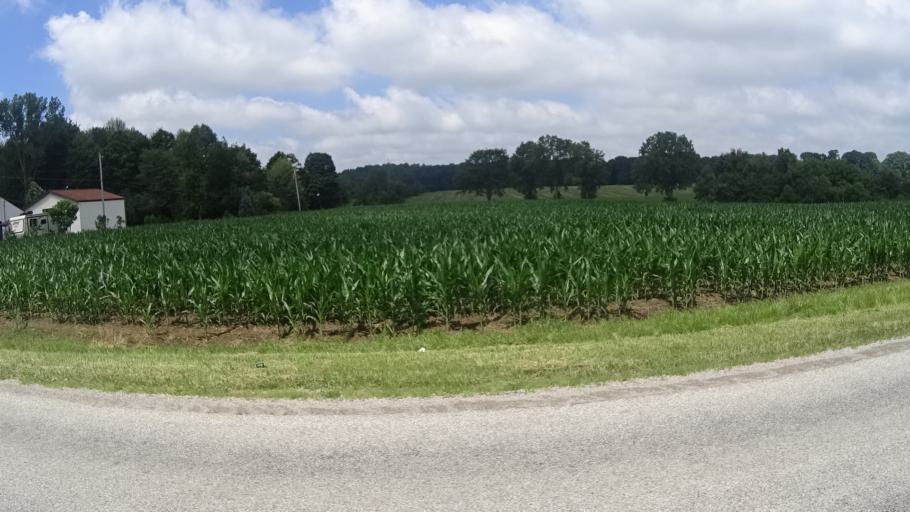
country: US
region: Ohio
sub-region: Huron County
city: Wakeman
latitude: 41.3097
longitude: -82.3634
